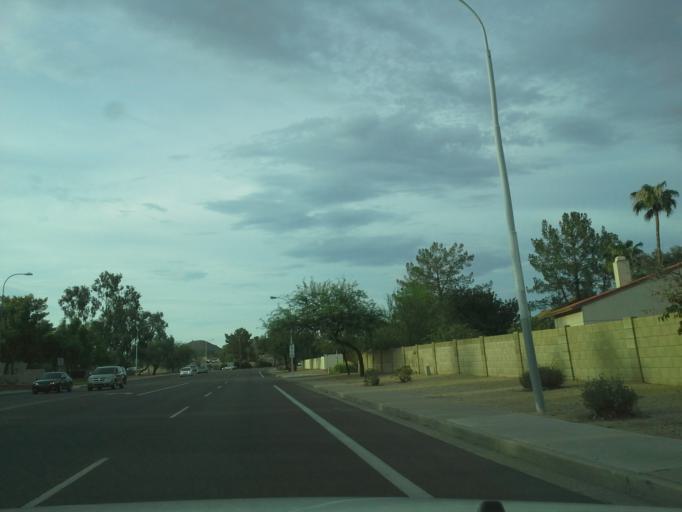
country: US
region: Arizona
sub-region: Maricopa County
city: Guadalupe
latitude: 33.3497
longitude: -111.9804
